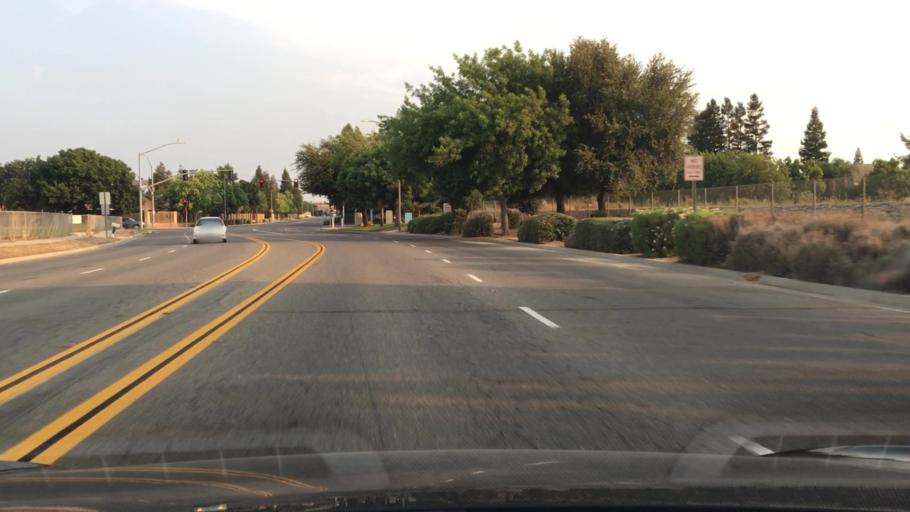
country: US
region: California
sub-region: Fresno County
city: Clovis
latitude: 36.8458
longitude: -119.6931
